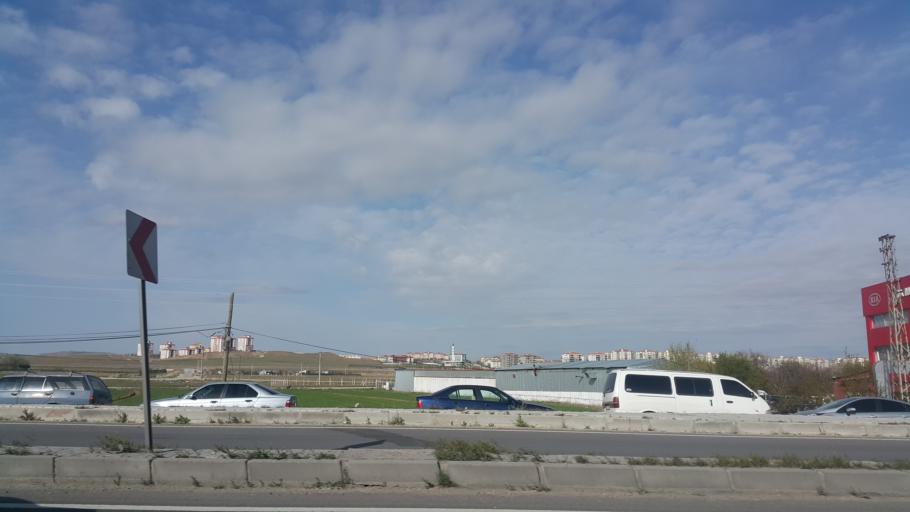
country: TR
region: Aksaray
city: Aksaray
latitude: 38.4112
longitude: 33.9751
